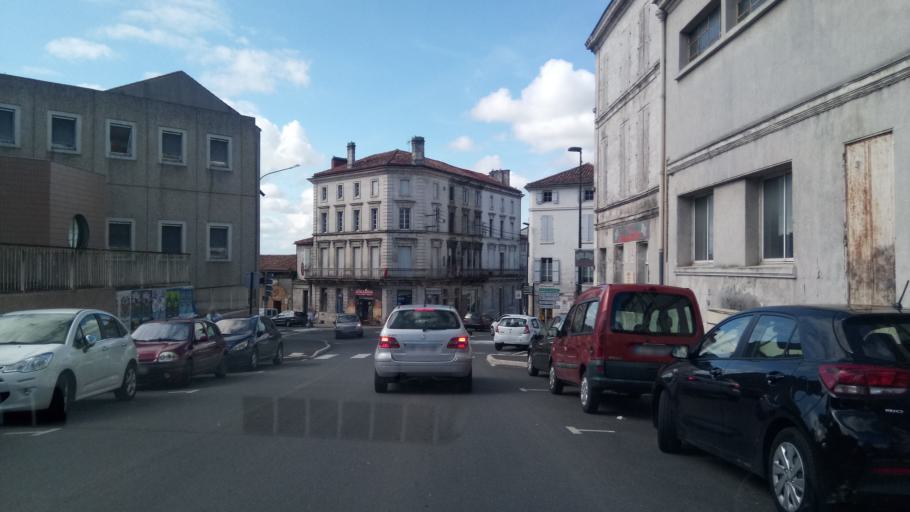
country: FR
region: Poitou-Charentes
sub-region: Departement de la Charente
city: Angouleme
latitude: 45.6517
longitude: 0.1589
